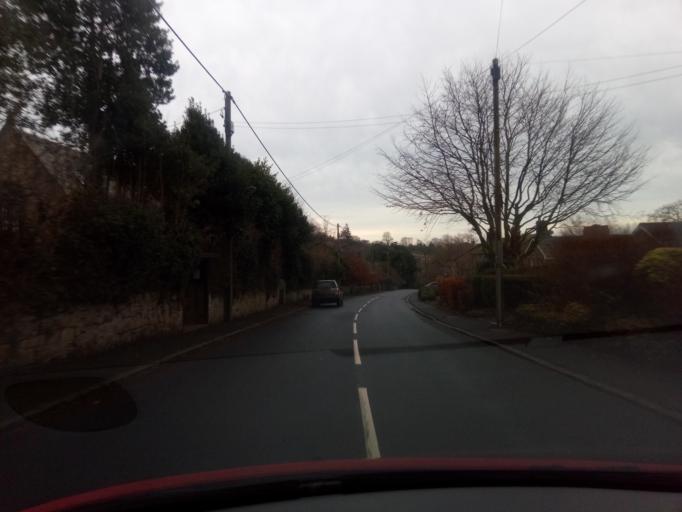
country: GB
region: England
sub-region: Northumberland
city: Whittingham
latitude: 55.4694
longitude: -1.8328
